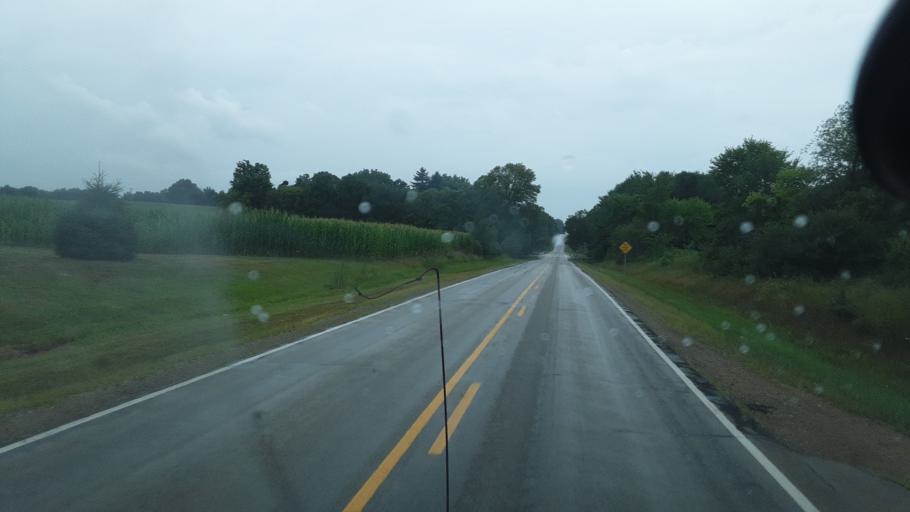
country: US
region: Indiana
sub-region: Steuben County
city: Hamilton
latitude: 41.5590
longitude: -84.8319
